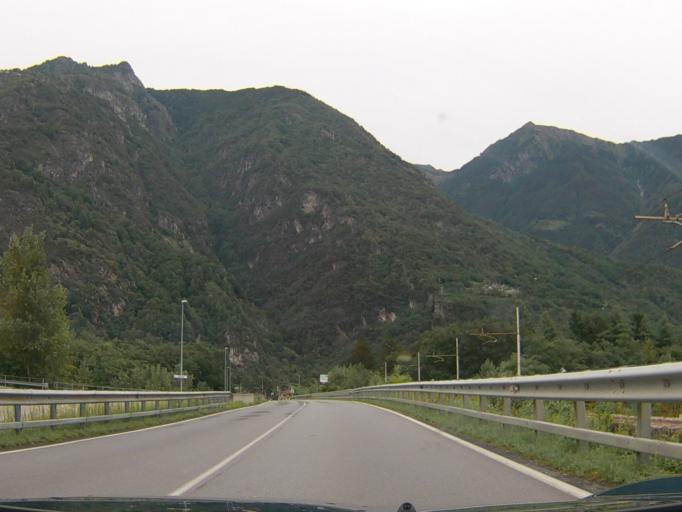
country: IT
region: Lombardy
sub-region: Provincia di Sondrio
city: Novate Mezzola
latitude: 46.2106
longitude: 9.4516
